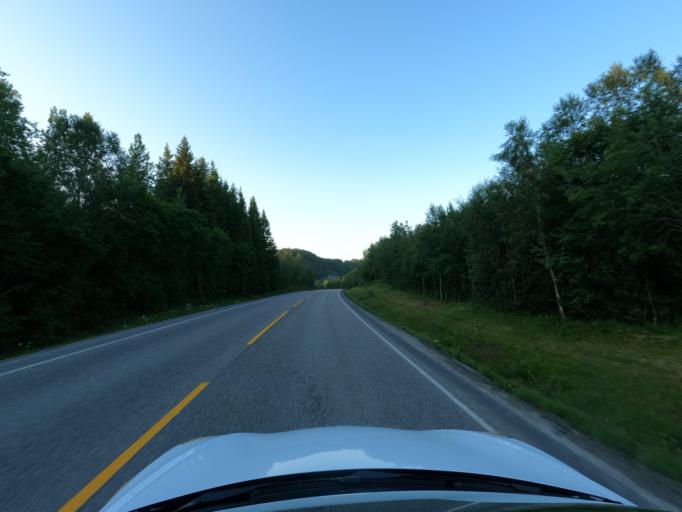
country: NO
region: Troms
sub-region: Harstad
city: Harstad
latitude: 68.7255
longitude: 16.5383
